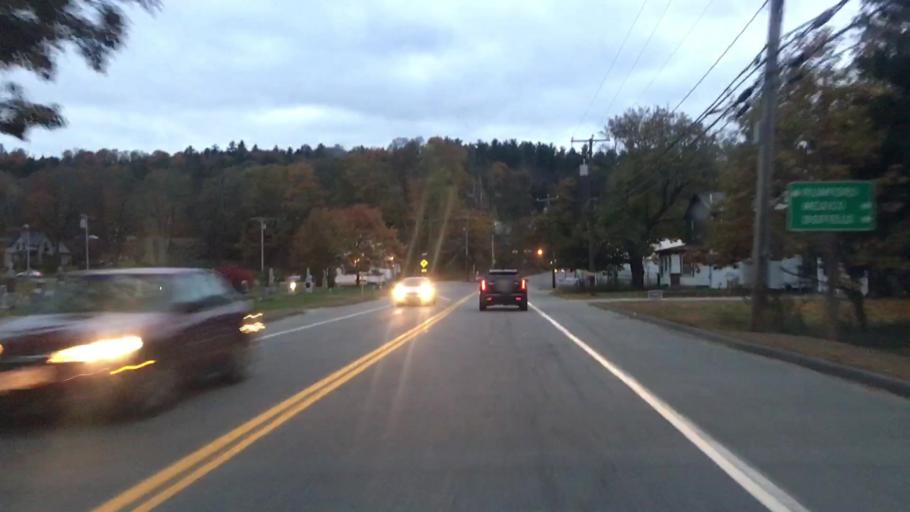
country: US
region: Maine
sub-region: Oxford County
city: Dixfield
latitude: 44.5261
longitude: -70.4622
